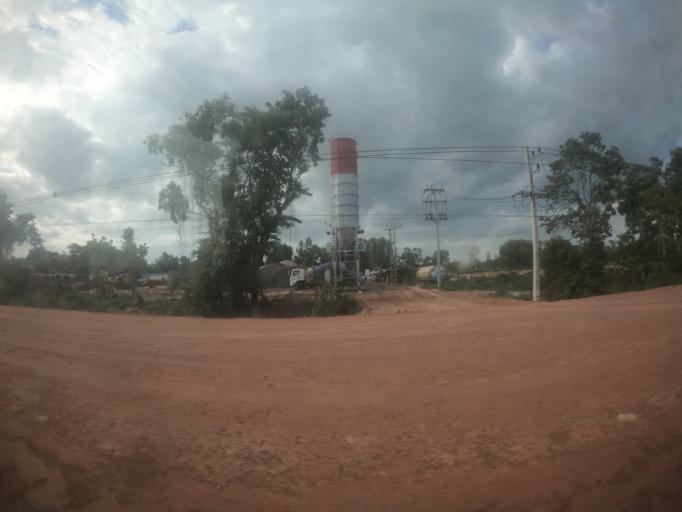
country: TH
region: Surin
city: Kap Choeng
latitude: 14.4678
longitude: 103.6287
